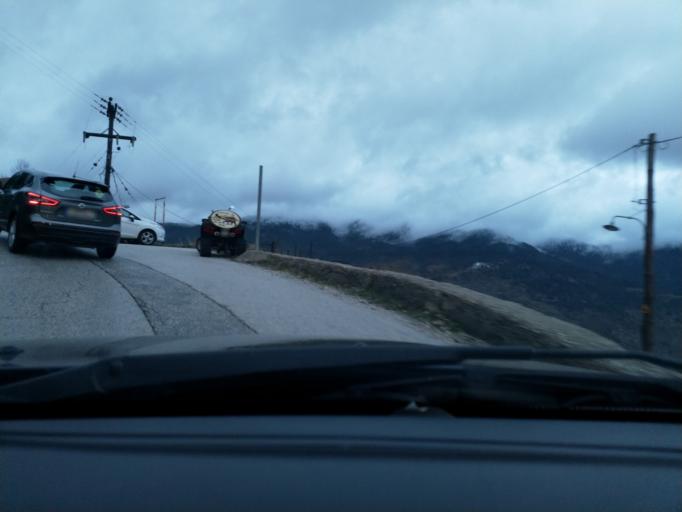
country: GR
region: Epirus
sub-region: Nomos Ioanninon
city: Metsovo
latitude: 39.7657
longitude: 21.1788
